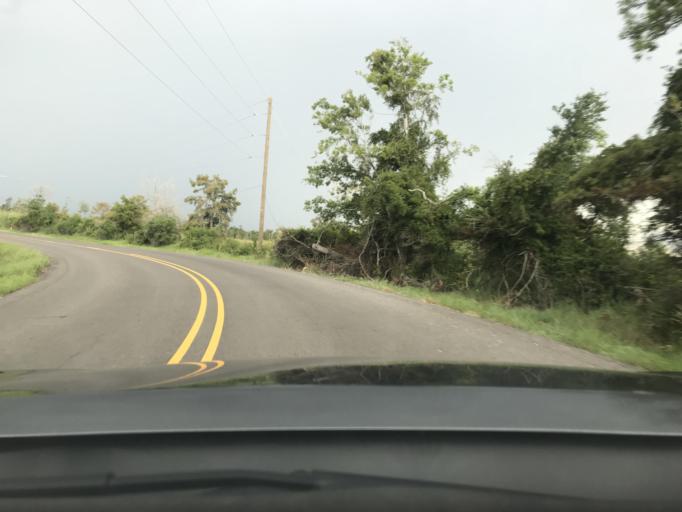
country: US
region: Louisiana
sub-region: Calcasieu Parish
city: Westlake
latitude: 30.2569
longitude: -93.2188
